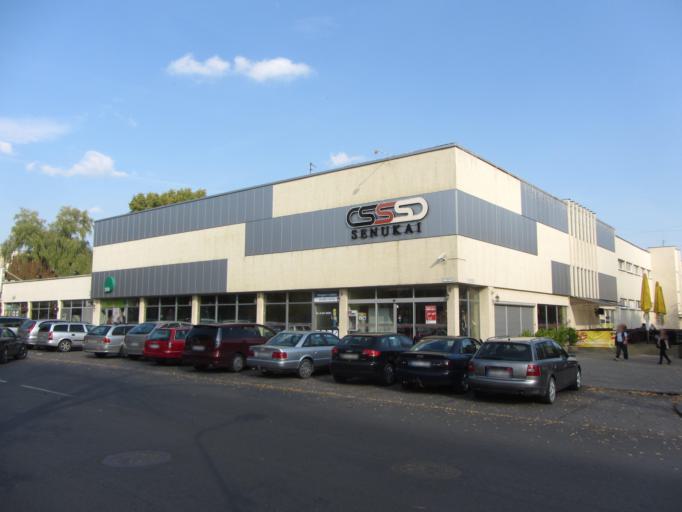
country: LT
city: Trakai
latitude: 54.6377
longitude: 24.9340
